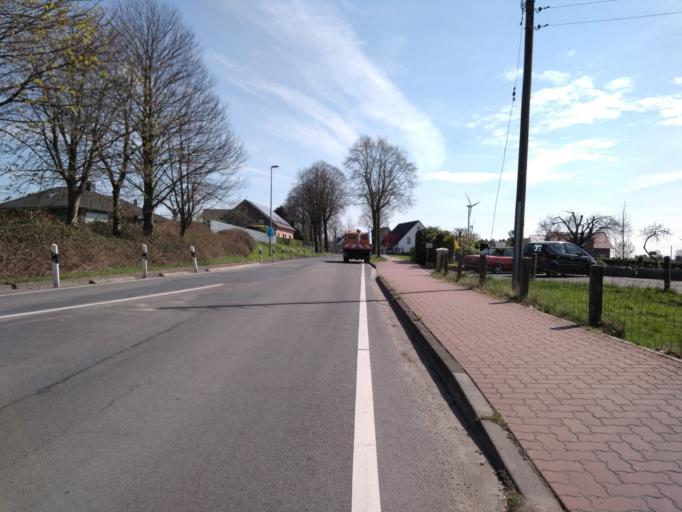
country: DE
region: North Rhine-Westphalia
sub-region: Regierungsbezirk Dusseldorf
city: Schermbeck
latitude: 51.6648
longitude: 6.8790
